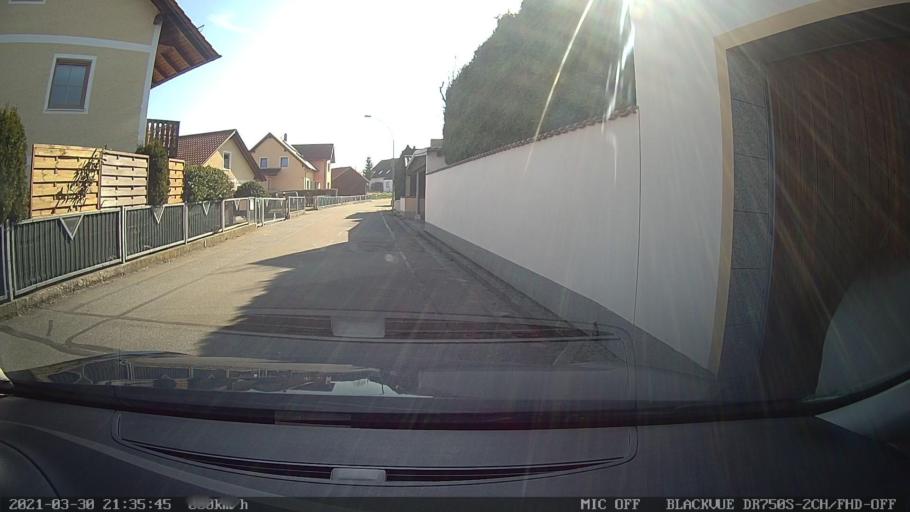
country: DE
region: Bavaria
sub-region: Upper Palatinate
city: Zeitlarn
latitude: 49.0997
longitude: 12.1006
